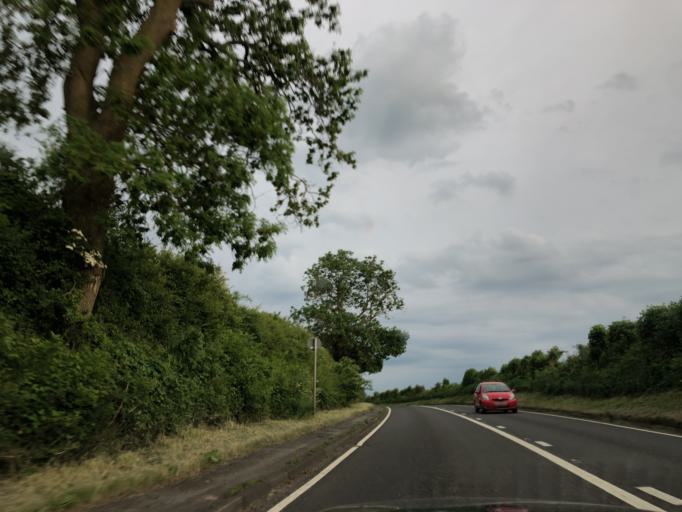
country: GB
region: England
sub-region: Warwickshire
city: Wroxall
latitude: 52.3141
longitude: -1.6663
